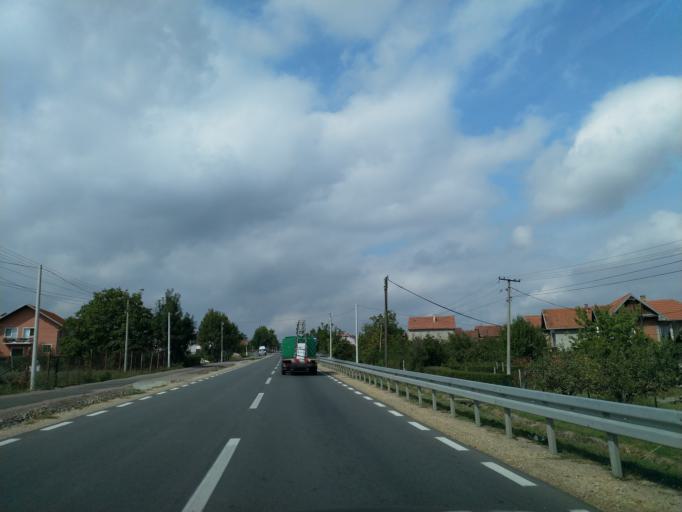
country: RS
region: Central Serbia
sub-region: Sumadijski Okrug
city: Kragujevac
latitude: 44.0674
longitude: 20.8809
